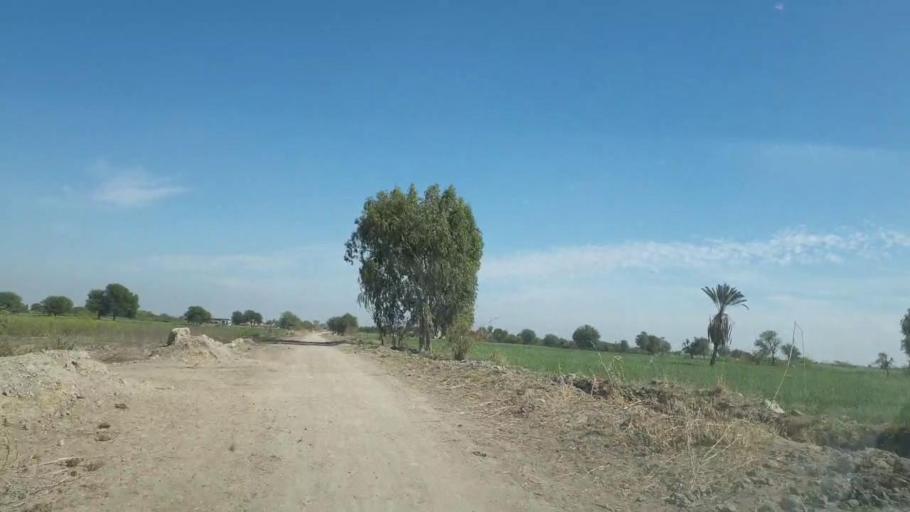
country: PK
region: Sindh
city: Pithoro
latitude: 25.6070
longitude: 69.2795
